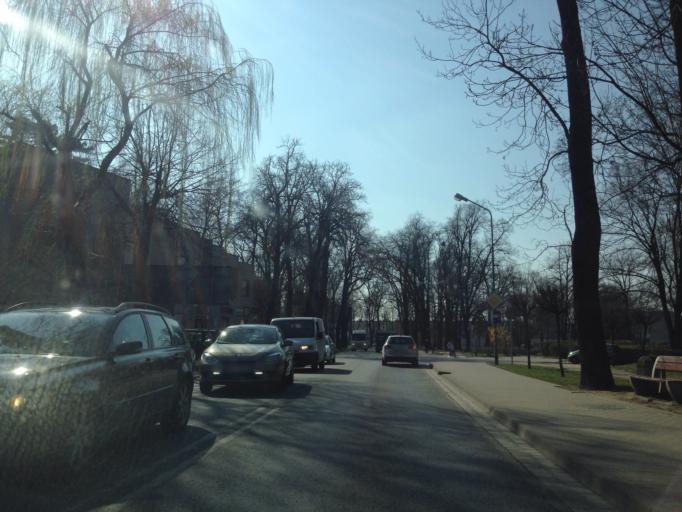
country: PL
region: Lower Silesian Voivodeship
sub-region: Powiat olesnicki
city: Olesnica
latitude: 51.2102
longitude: 17.3935
